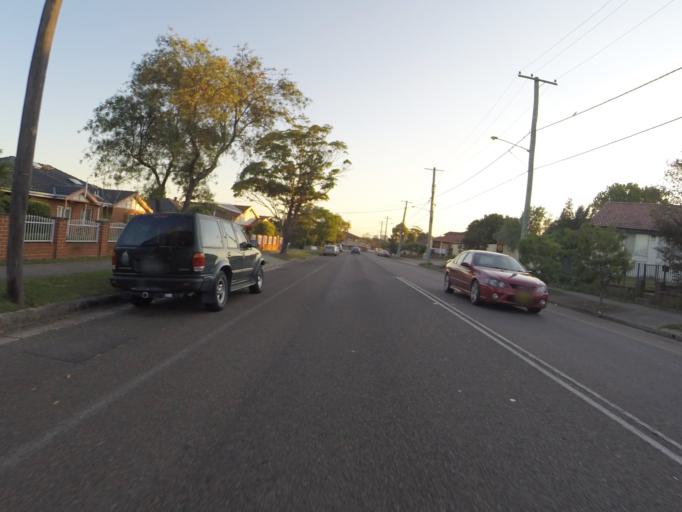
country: AU
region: New South Wales
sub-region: Rockdale
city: Bexley
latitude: -33.9448
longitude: 151.1138
